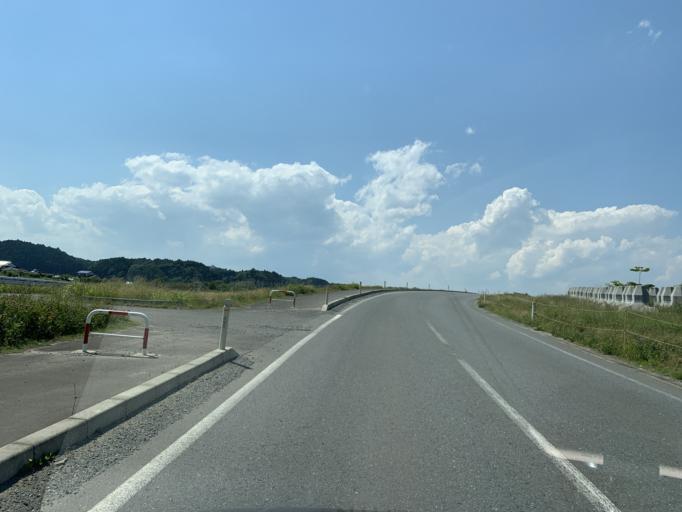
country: JP
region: Miyagi
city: Yamoto
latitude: 38.3877
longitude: 141.1624
